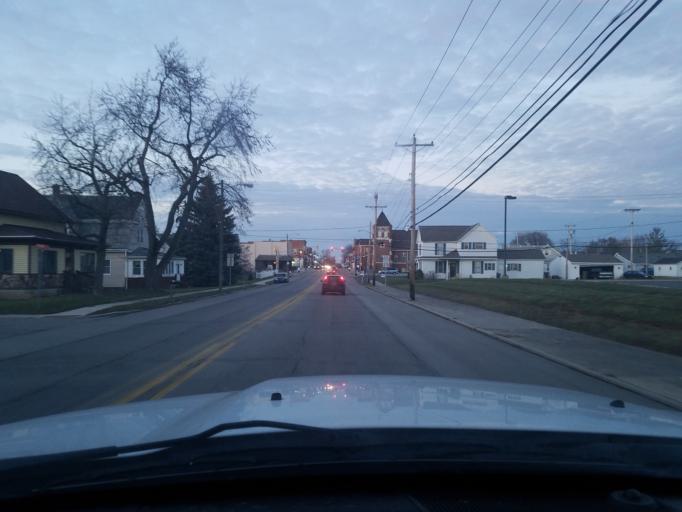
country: US
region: Indiana
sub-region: Wells County
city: Ossian
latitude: 40.8781
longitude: -85.1667
